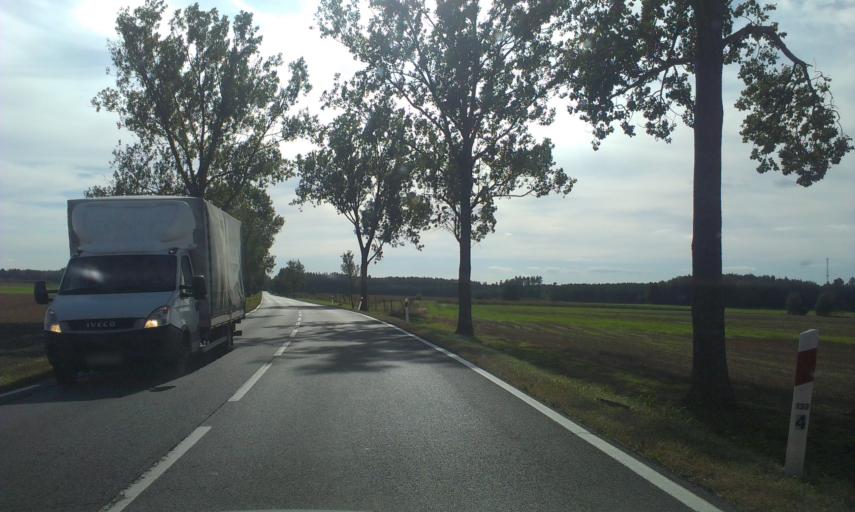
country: PL
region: Greater Poland Voivodeship
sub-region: Powiat zlotowski
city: Okonek
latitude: 53.5608
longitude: 16.8342
